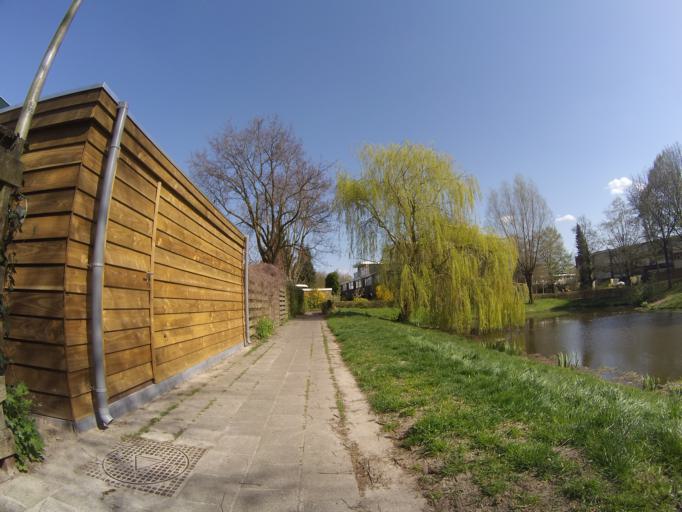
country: NL
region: Utrecht
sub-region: Gemeente Amersfoort
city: Hoogland
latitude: 52.1907
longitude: 5.3705
